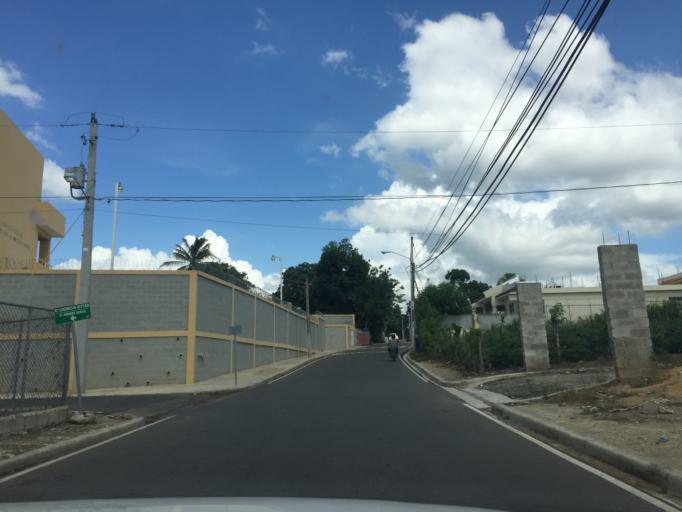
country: DO
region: Santiago
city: Licey al Medio
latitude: 19.3786
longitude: -70.6013
